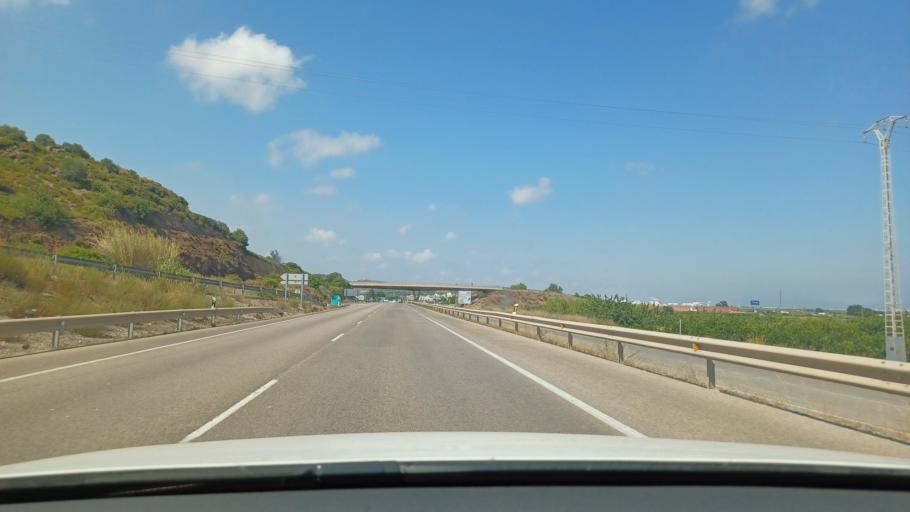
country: ES
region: Valencia
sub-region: Provincia de Castello
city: Almenara
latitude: 39.7571
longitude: -0.2134
